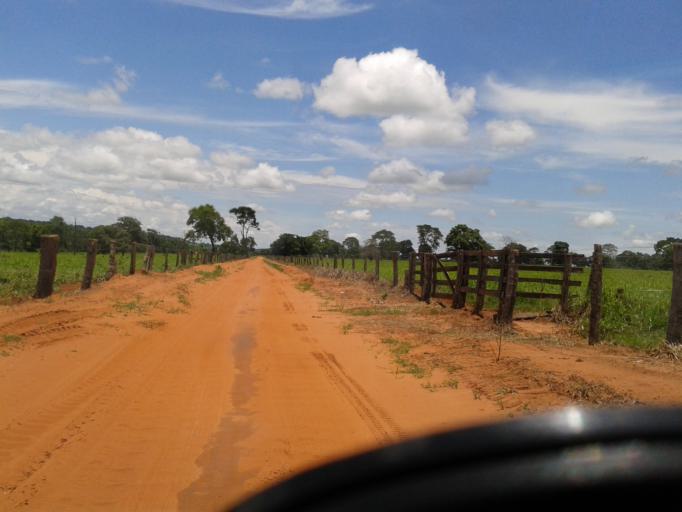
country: BR
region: Minas Gerais
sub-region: Santa Vitoria
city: Santa Vitoria
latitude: -18.9411
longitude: -49.8605
